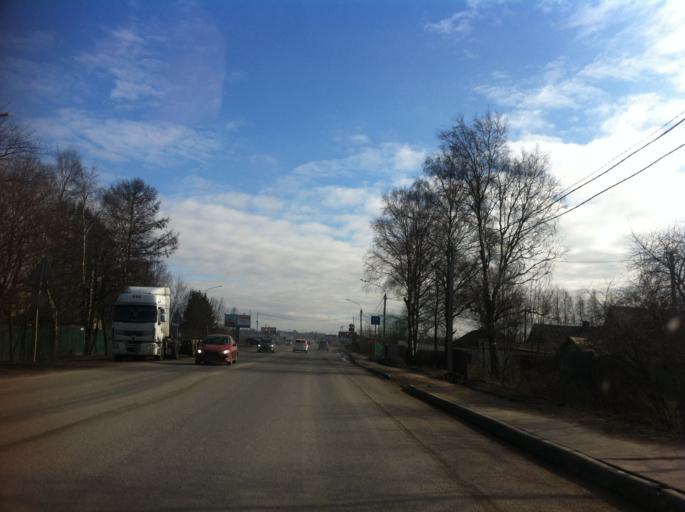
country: RU
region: Leningrad
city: Yanino Vtoroye
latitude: 59.9461
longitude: 30.5718
